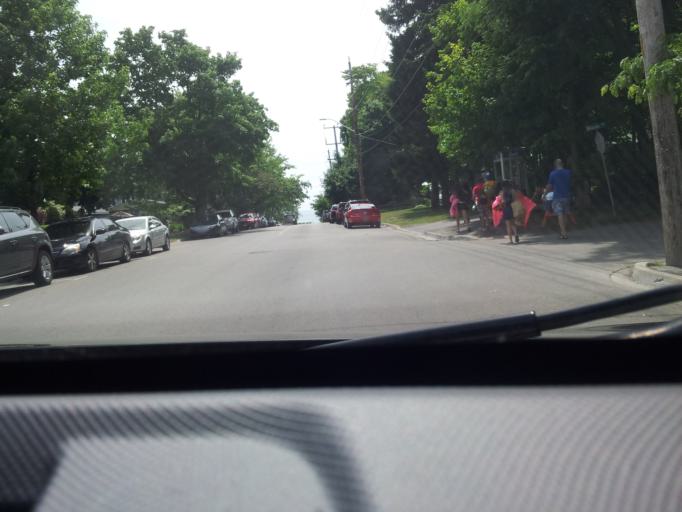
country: CA
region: Ontario
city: Norfolk County
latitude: 42.7851
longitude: -80.2035
